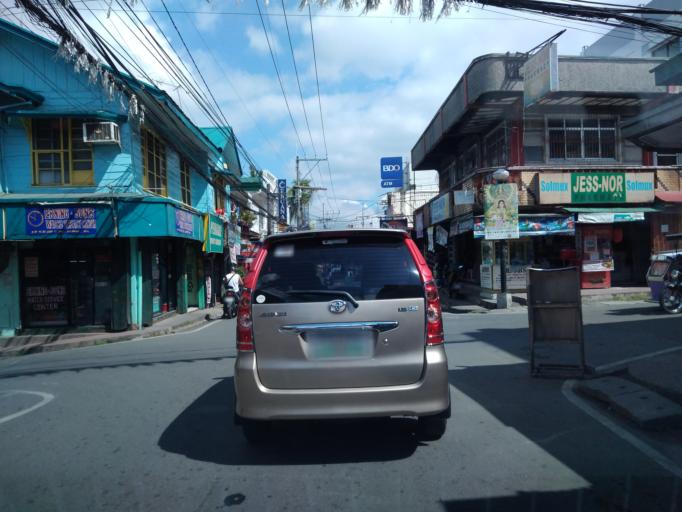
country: PH
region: Central Luzon
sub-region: Province of Bulacan
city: Santa Maria
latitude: 14.8198
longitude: 120.9621
